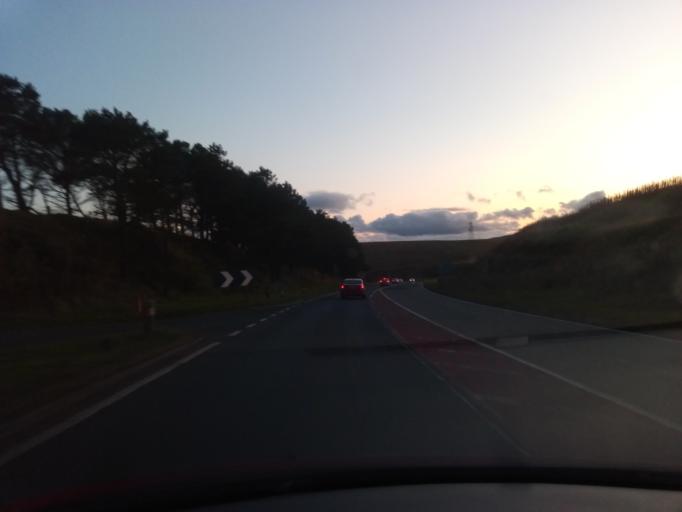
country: GB
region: Scotland
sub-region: East Lothian
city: Pencaitland
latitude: 55.8038
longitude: -2.8354
